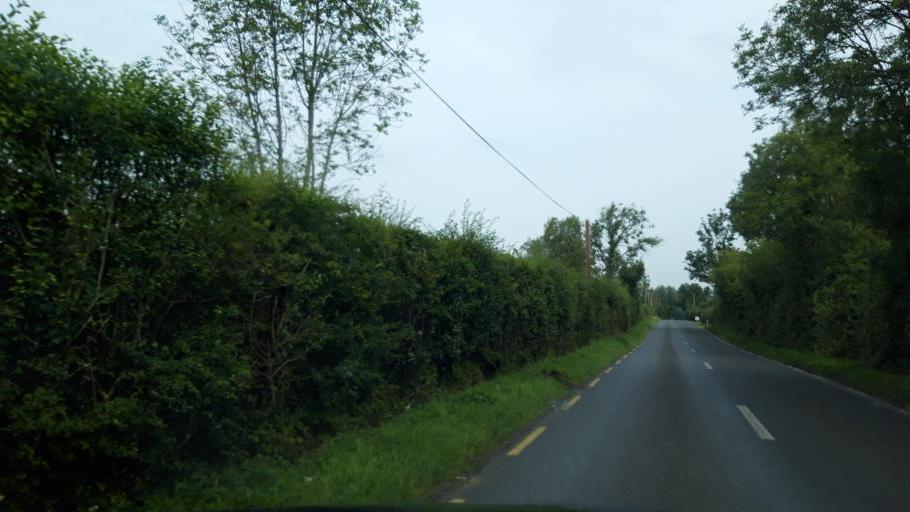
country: IE
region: Leinster
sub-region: Kilkenny
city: Callan
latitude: 52.5361
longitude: -7.5214
